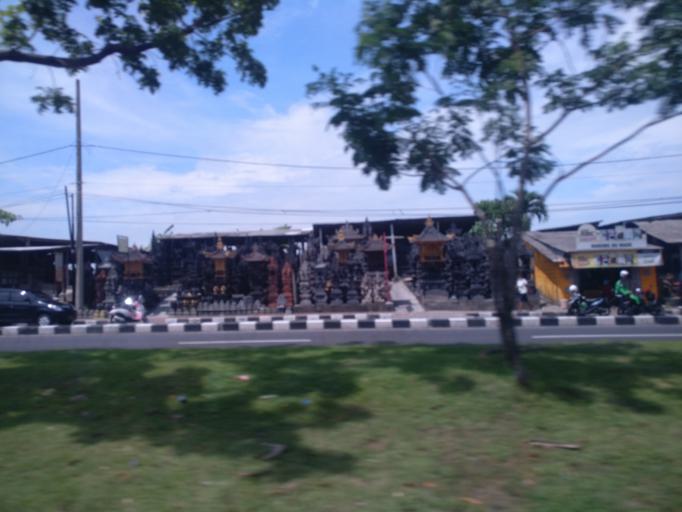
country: ID
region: Bali
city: Banjar Kertajiwa
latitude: -8.6496
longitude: 115.2599
